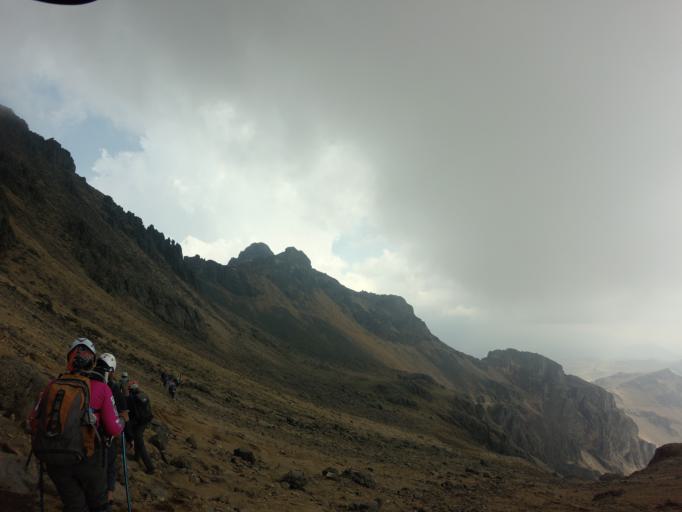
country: MX
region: Mexico
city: Amecameca de Juarez
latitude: 19.1517
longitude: -98.6400
